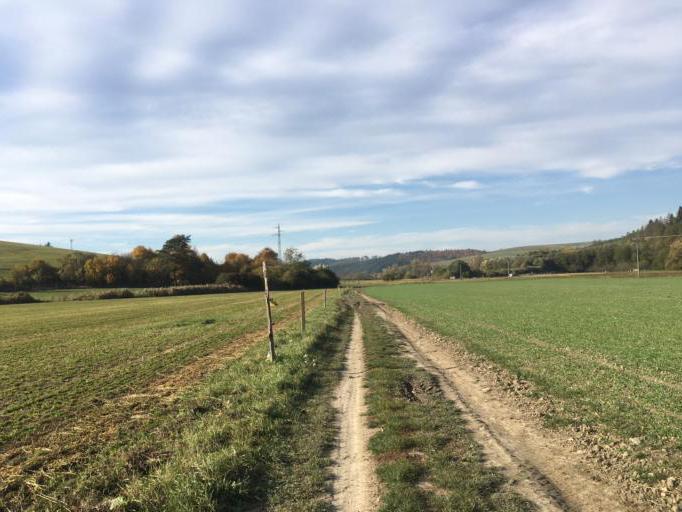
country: SK
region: Trenciansky
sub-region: Okres Povazska Bystrica
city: Povazska Bystrica
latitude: 49.0412
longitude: 18.4295
